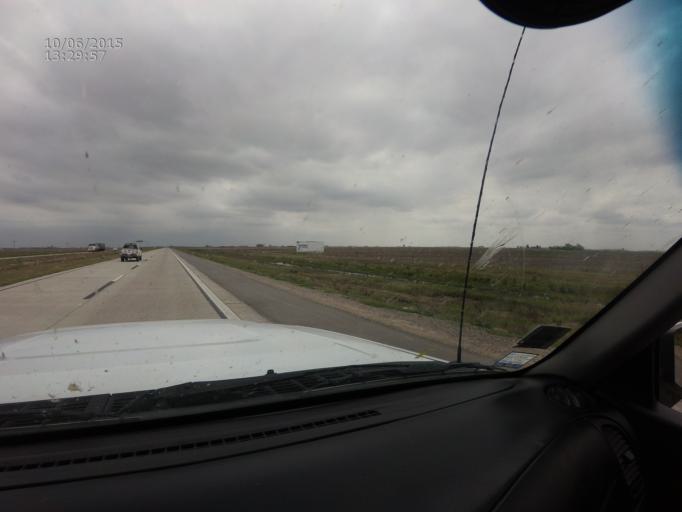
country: AR
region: Cordoba
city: Leones
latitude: -32.6365
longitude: -62.2546
